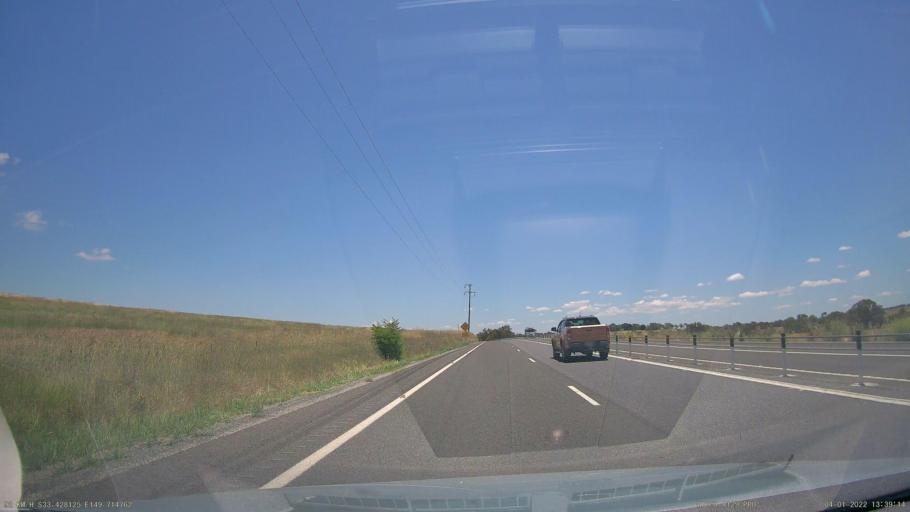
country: AU
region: New South Wales
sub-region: Bathurst Regional
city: Kelso
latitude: -33.4279
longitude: 149.7153
